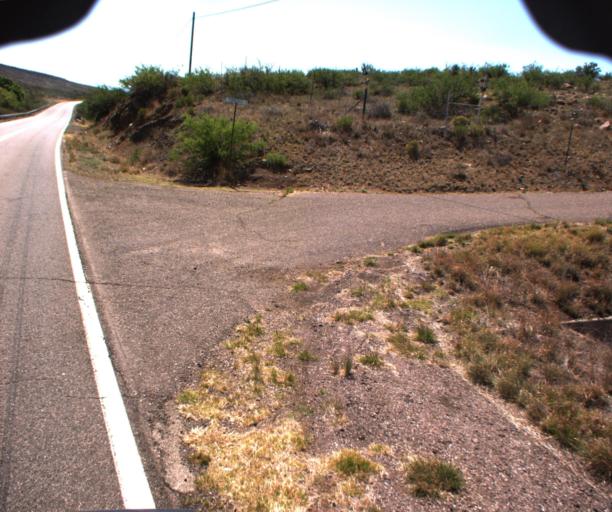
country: US
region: Arizona
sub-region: Cochise County
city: Douglas
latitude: 31.4784
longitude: -109.4007
